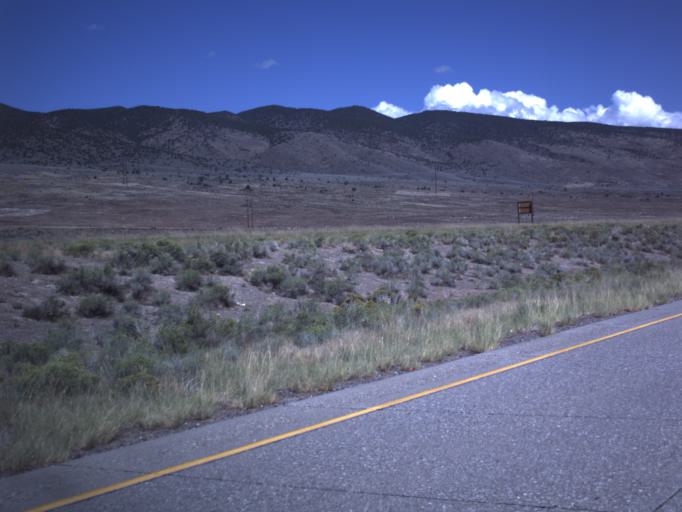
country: US
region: Utah
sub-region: Sevier County
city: Monroe
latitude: 38.6343
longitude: -112.2222
